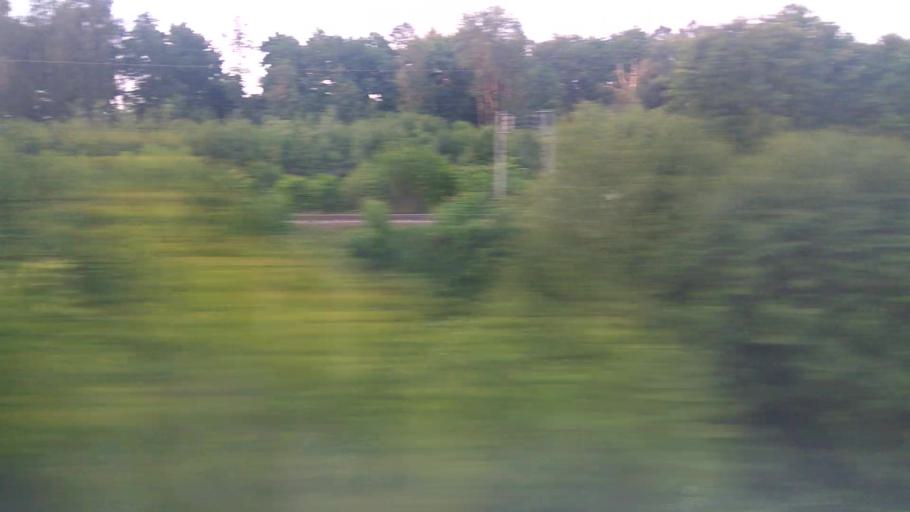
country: RU
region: Moskovskaya
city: Belyye Stolby
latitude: 55.3048
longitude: 37.8760
